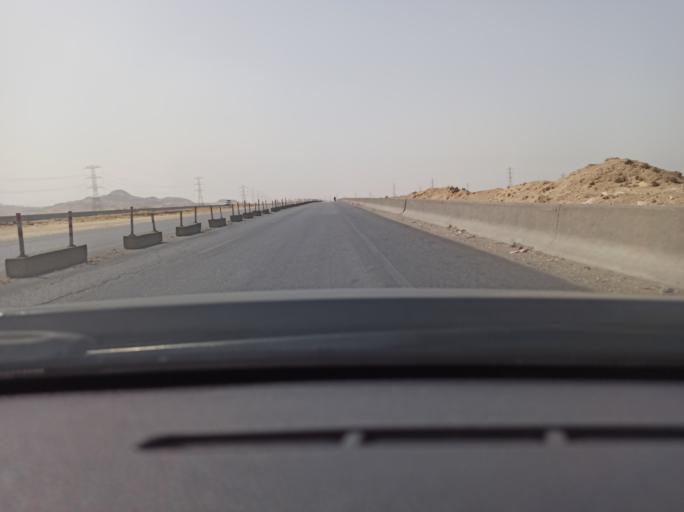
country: EG
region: Muhafazat Bani Suwayf
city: Bush
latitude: 29.1433
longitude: 31.2297
